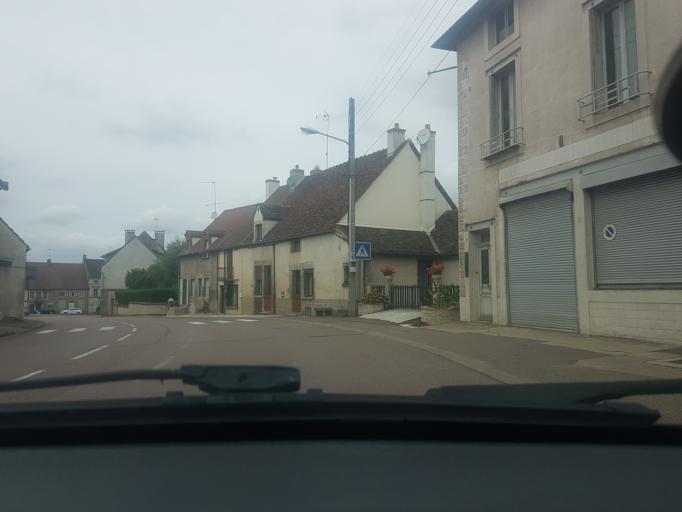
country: FR
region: Bourgogne
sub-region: Departement de la Cote-d'Or
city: Arnay-le-Duc
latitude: 47.1337
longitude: 4.4874
